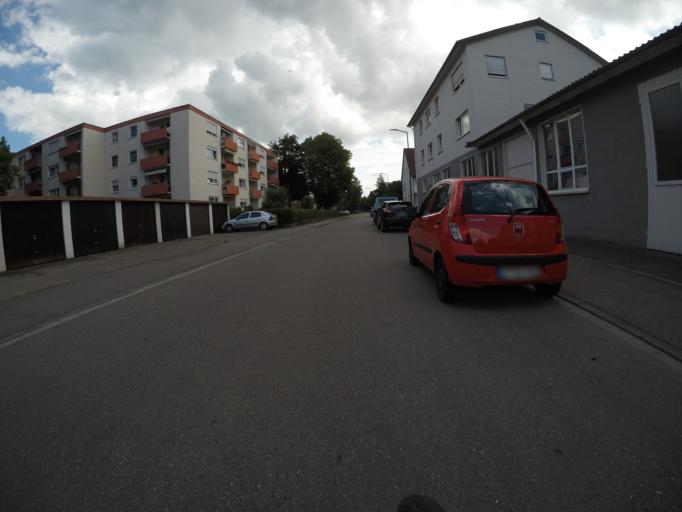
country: DE
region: Baden-Wuerttemberg
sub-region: Regierungsbezirk Stuttgart
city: Eislingen
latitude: 48.7001
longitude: 9.7144
